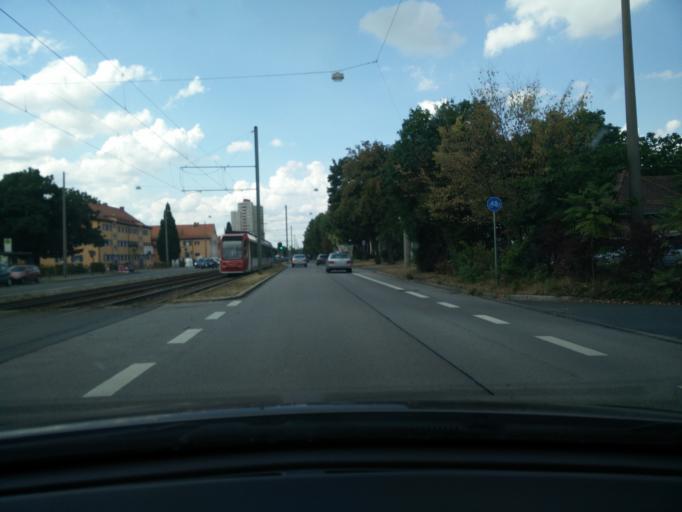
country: DE
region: Bavaria
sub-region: Regierungsbezirk Mittelfranken
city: Nuernberg
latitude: 49.4099
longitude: 11.0837
